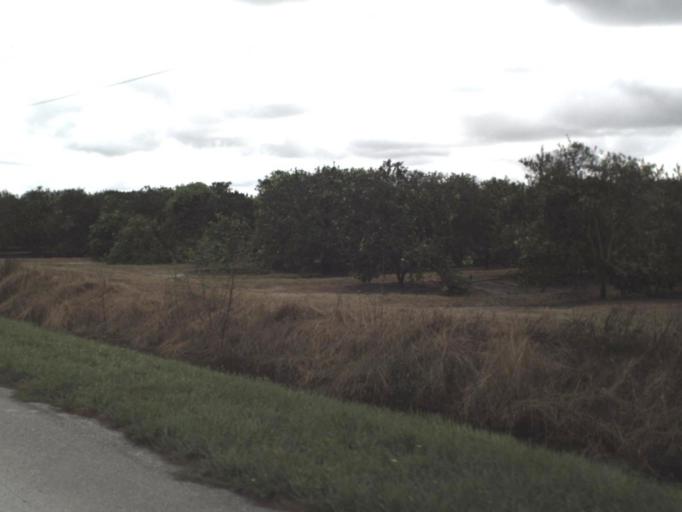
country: US
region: Florida
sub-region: Hillsborough County
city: Wimauma
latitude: 27.5887
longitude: -82.1026
